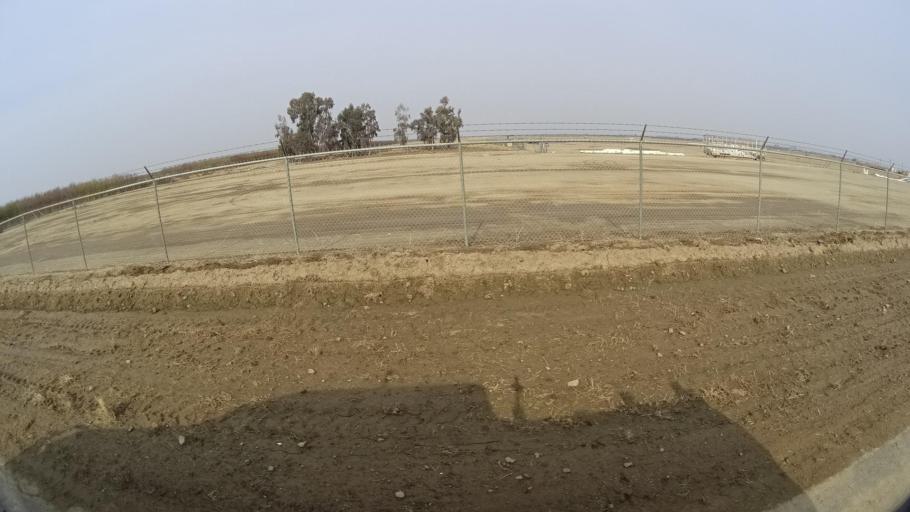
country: US
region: California
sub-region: Kern County
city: Arvin
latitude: 35.1795
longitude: -118.8590
